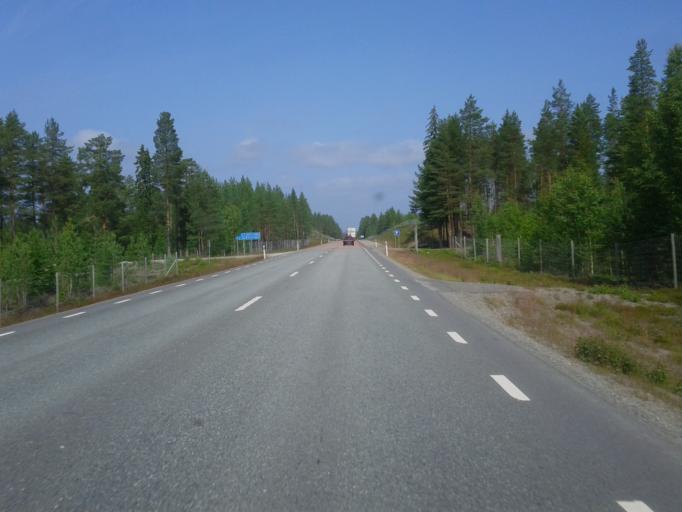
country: SE
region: Vaesterbotten
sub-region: Skelleftea Kommun
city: Burea
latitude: 64.5913
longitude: 21.2131
